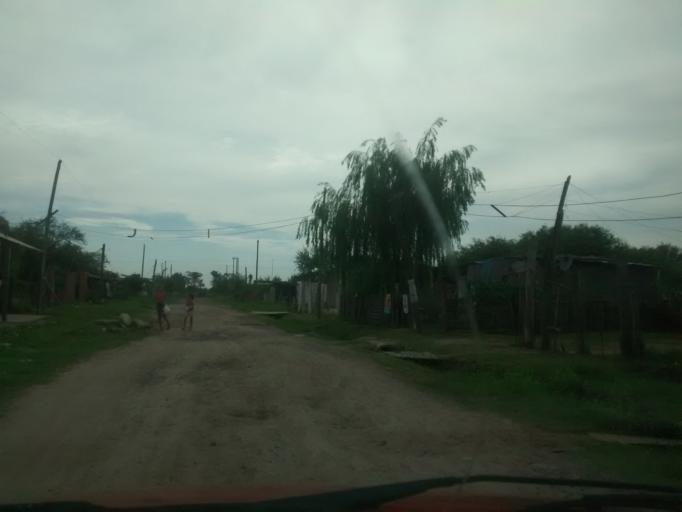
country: AR
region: Chaco
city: Fontana
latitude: -27.4643
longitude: -59.0314
